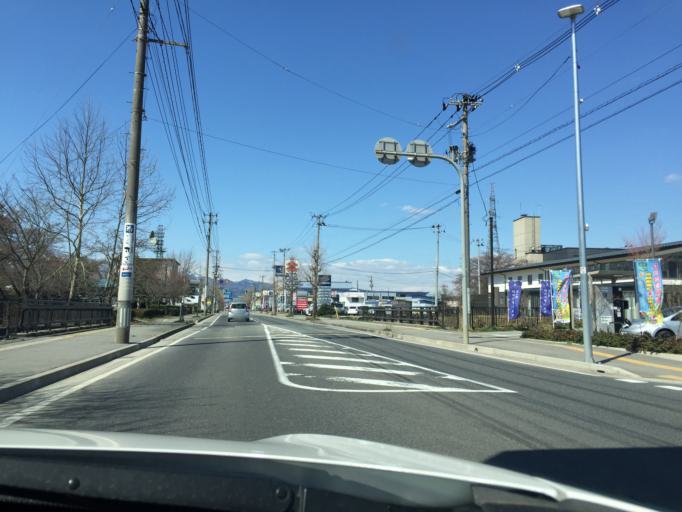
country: JP
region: Yamagata
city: Nagai
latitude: 38.1083
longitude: 140.0432
